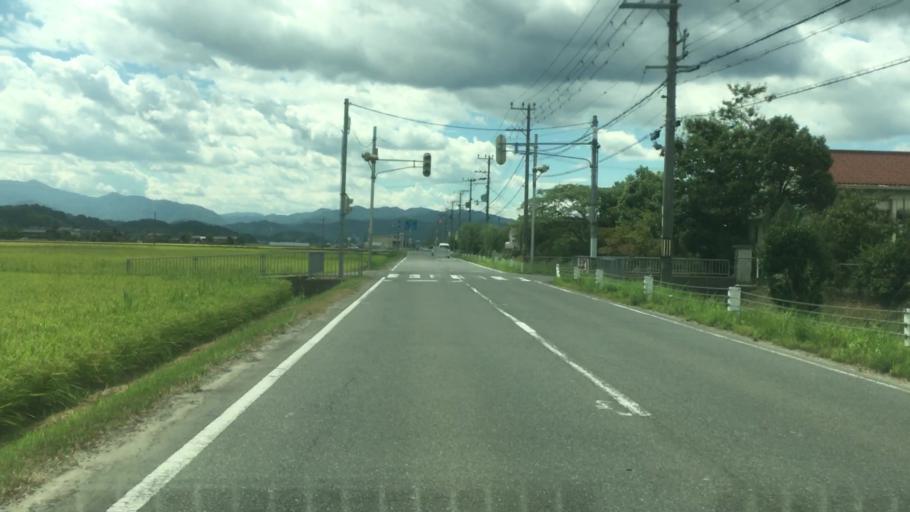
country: JP
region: Hyogo
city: Toyooka
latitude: 35.5302
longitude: 134.8398
